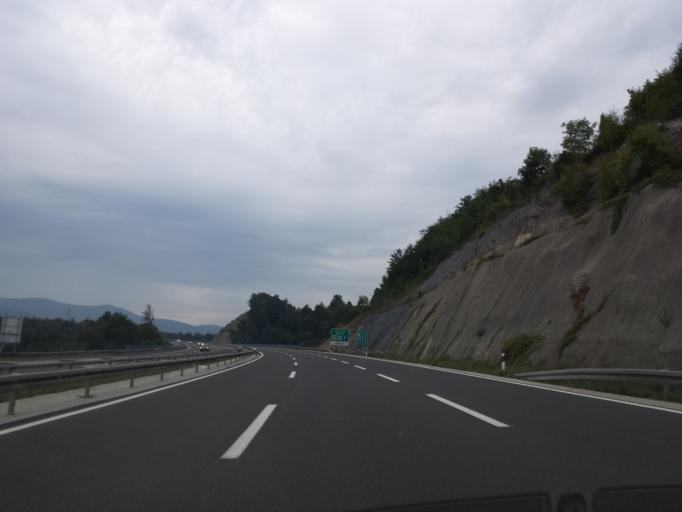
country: HR
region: Karlovacka
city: Ostarije
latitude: 45.1383
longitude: 15.2621
